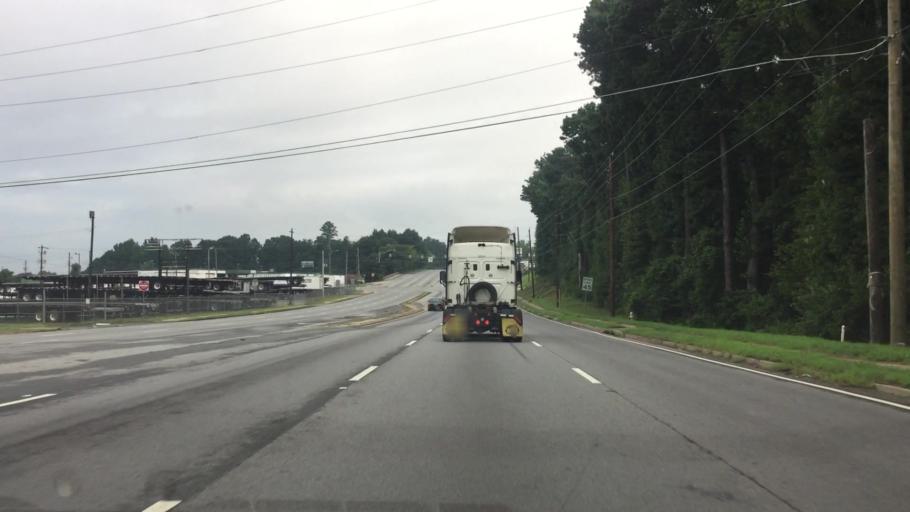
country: US
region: Georgia
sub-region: DeKalb County
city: Gresham Park
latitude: 33.6812
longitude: -84.3463
